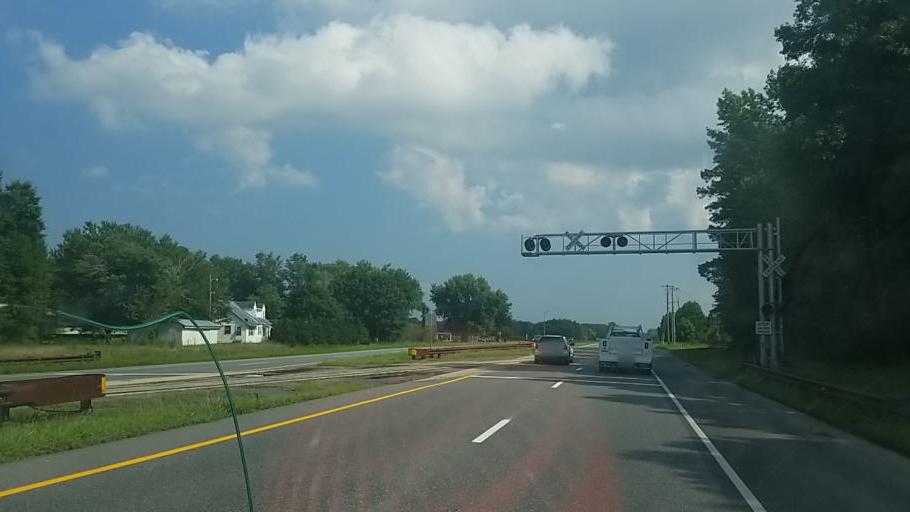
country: US
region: Delaware
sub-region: Sussex County
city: Selbyville
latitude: 38.4355
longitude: -75.2235
